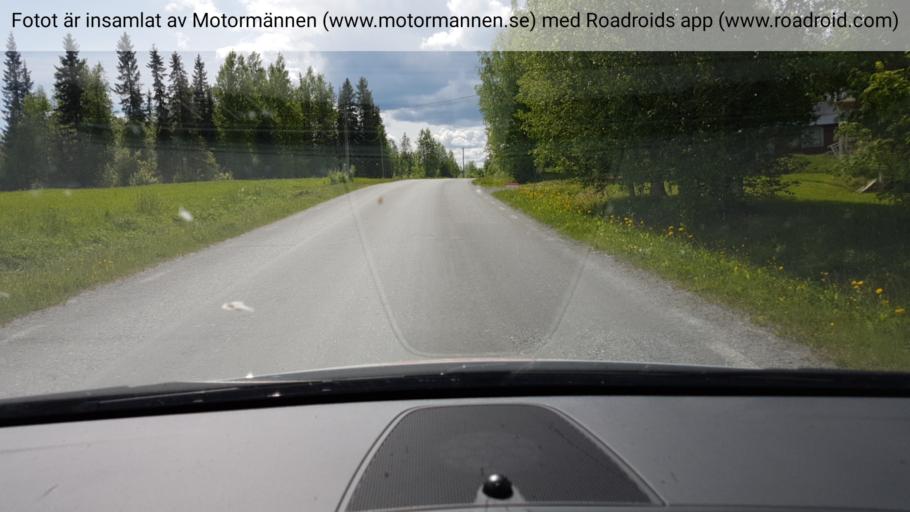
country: SE
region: Jaemtland
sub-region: Bergs Kommun
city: Hoverberg
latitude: 62.9801
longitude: 14.3233
